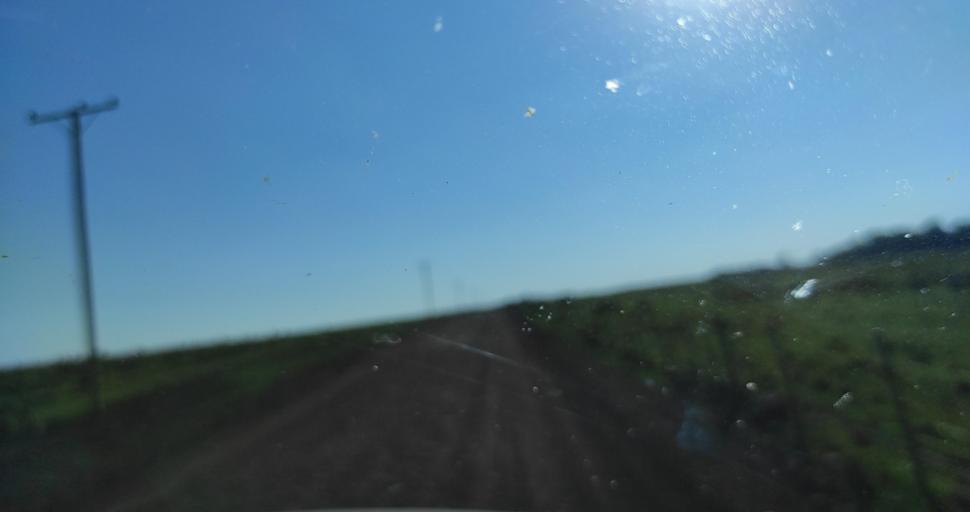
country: PY
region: Itapua
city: Carmen del Parana
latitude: -27.4109
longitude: -56.1481
